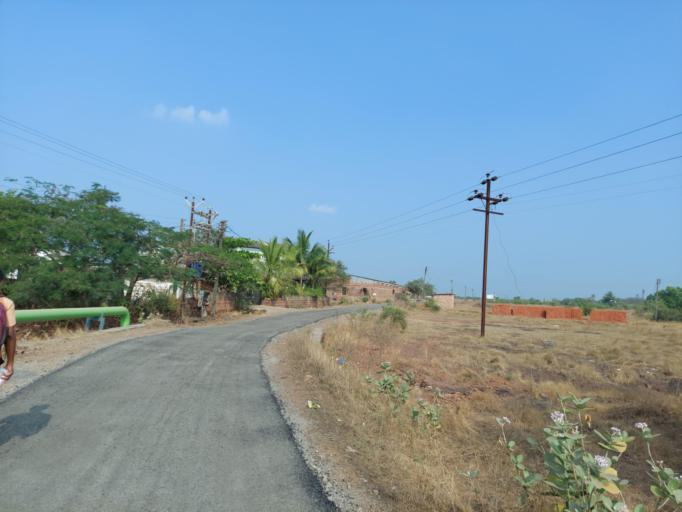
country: IN
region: Maharashtra
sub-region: Ratnagiri
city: Ratnagiri
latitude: 16.9323
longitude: 73.3243
